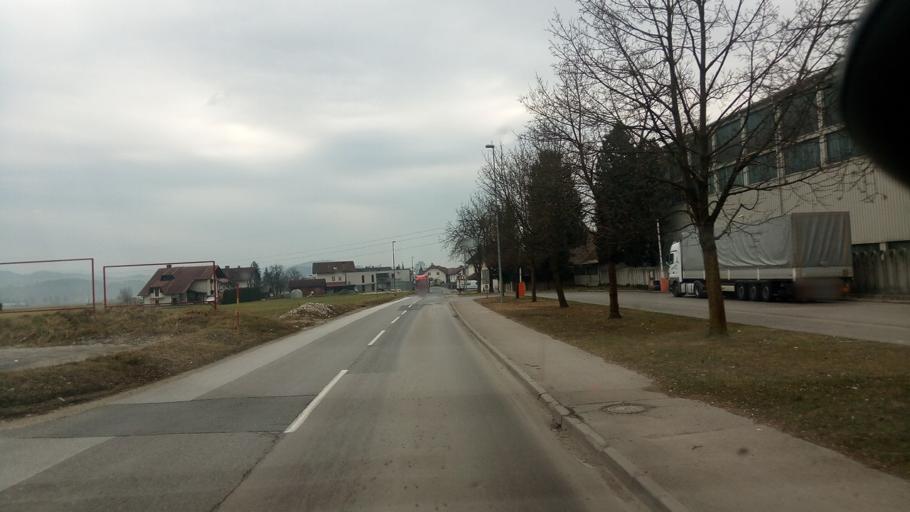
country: SI
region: Domzale
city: Vir
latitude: 46.1626
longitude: 14.6089
